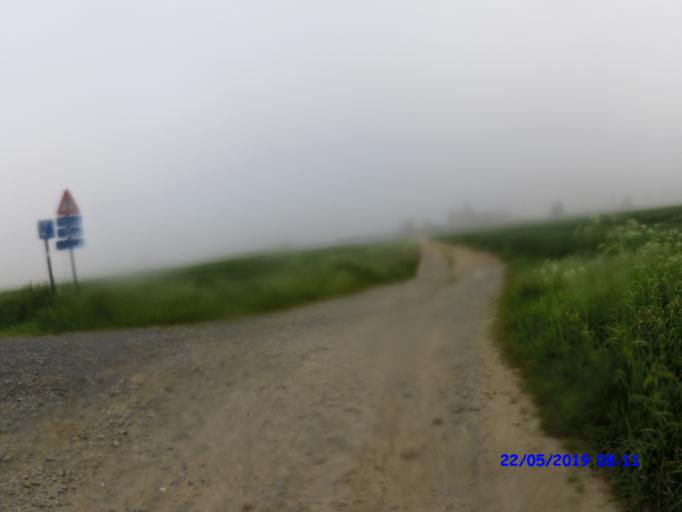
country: BE
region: Flanders
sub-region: Provincie Oost-Vlaanderen
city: Oudenaarde
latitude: 50.8193
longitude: 3.5968
